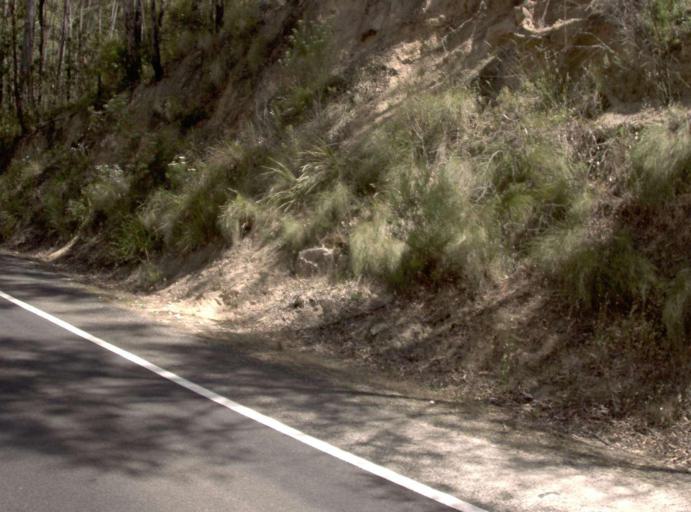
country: AU
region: New South Wales
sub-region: Bombala
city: Bombala
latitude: -37.5666
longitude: 149.2521
